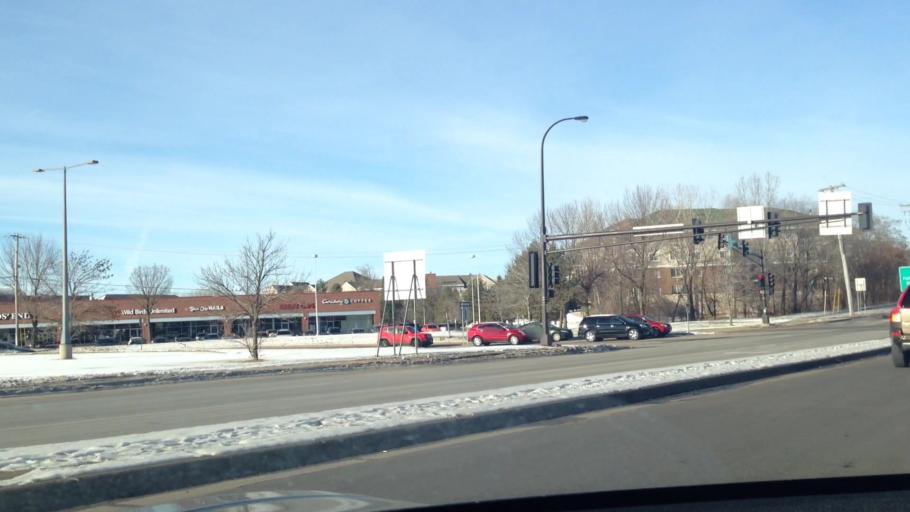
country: US
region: Minnesota
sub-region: Hennepin County
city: Minnetonka Mills
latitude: 44.9726
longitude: -93.4206
